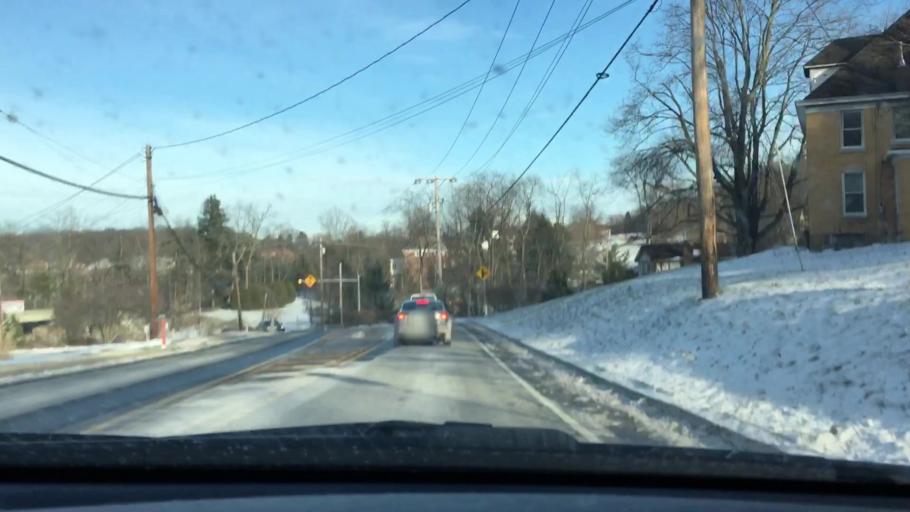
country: US
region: Pennsylvania
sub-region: Washington County
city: McMurray
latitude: 40.2772
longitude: -80.0854
